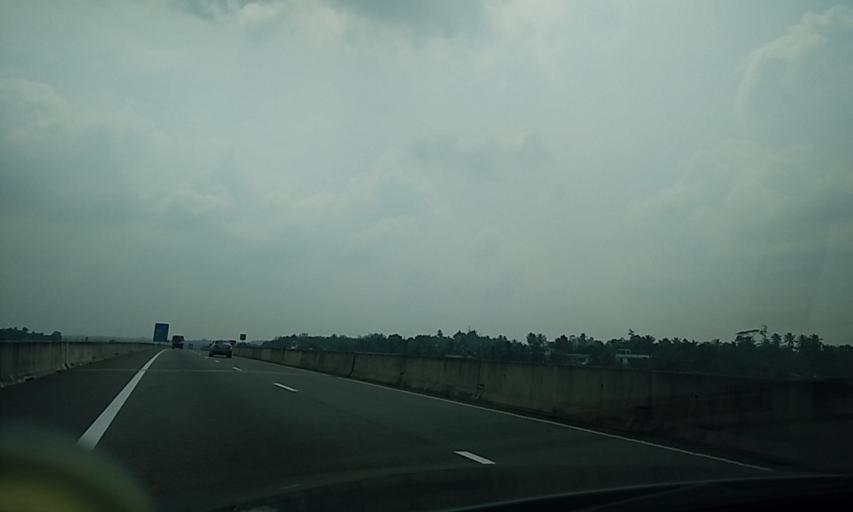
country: LK
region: Western
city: Homagama
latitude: 6.8966
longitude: 79.9789
